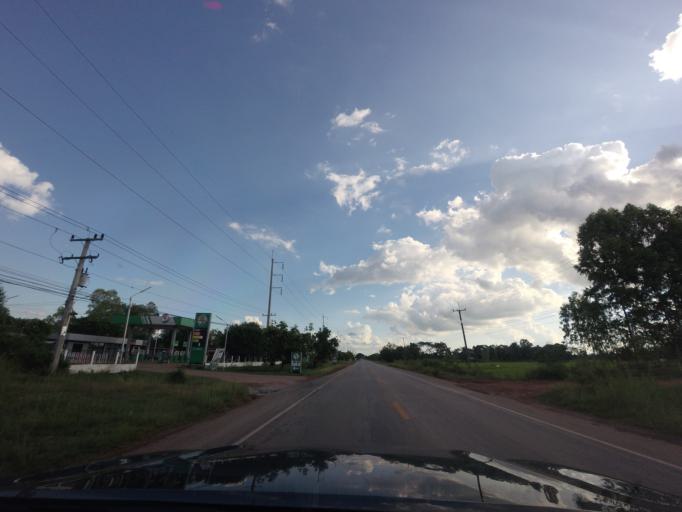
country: TH
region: Changwat Udon Thani
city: Thung Fon
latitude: 17.4789
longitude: 103.1951
